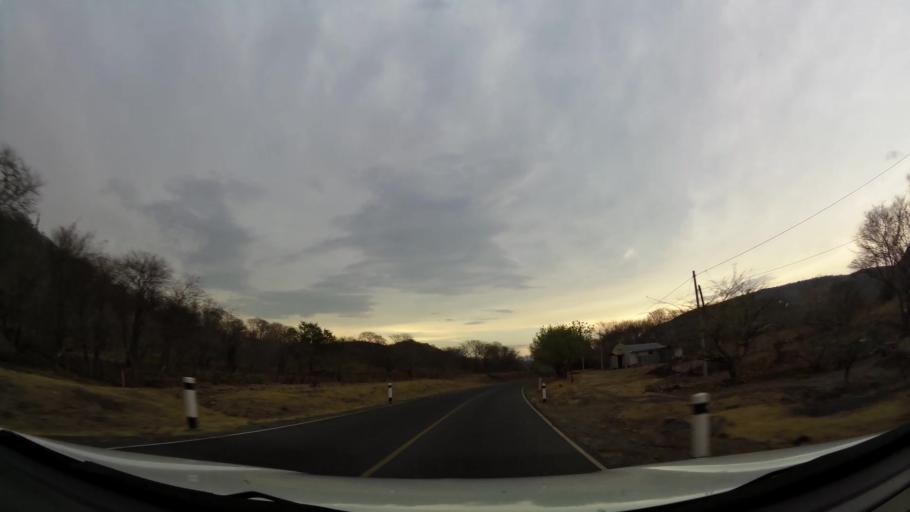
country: NI
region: Leon
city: La Jicaral
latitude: 12.6862
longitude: -86.4184
